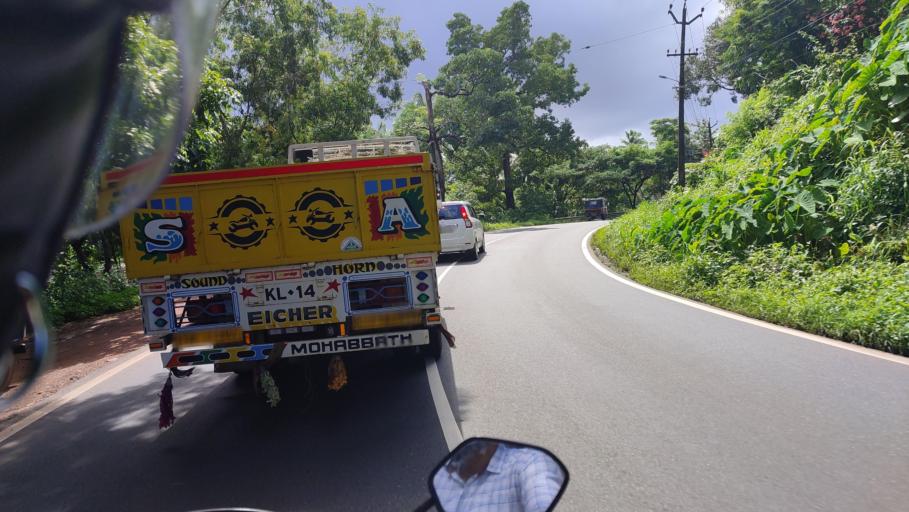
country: IN
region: Kerala
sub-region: Kasaragod District
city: Nileshwar
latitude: 12.2204
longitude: 75.1589
